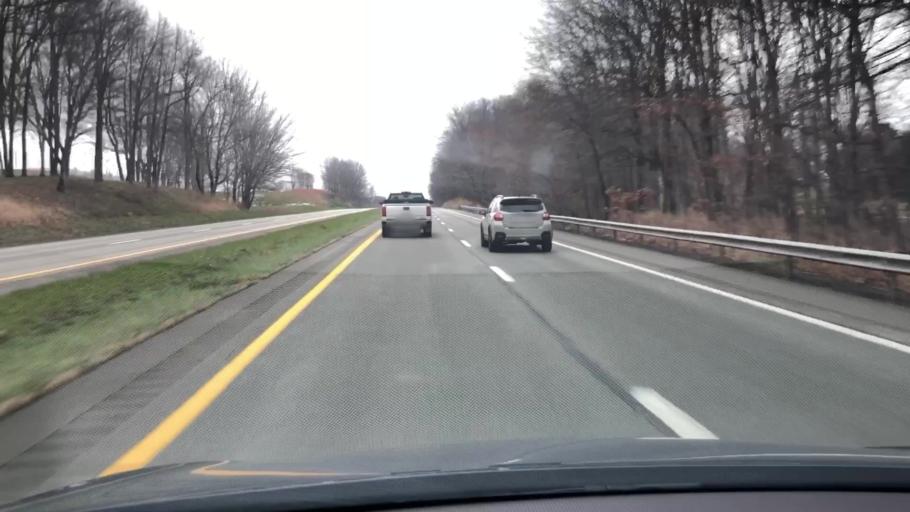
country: US
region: Pennsylvania
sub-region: Westmoreland County
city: Scottdale
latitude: 40.1005
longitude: -79.5570
